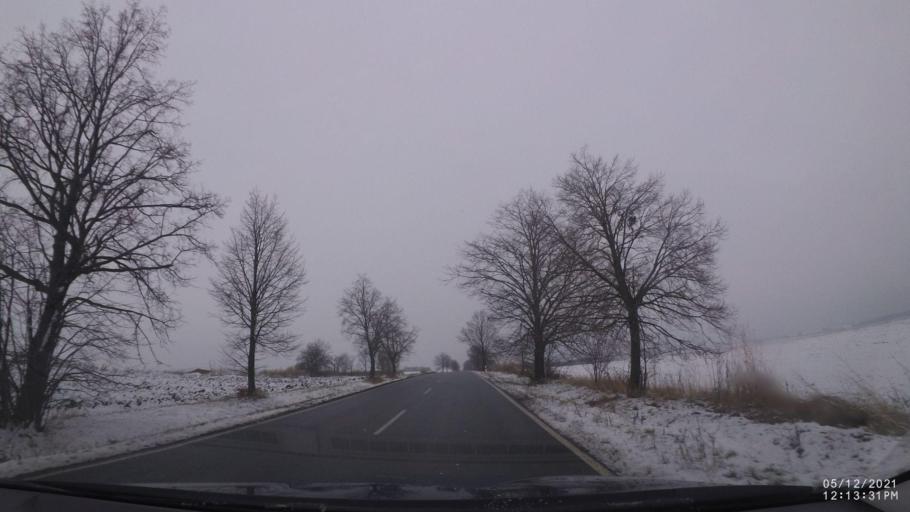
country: CZ
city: Ceske Mezirici
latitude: 50.3010
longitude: 16.0213
